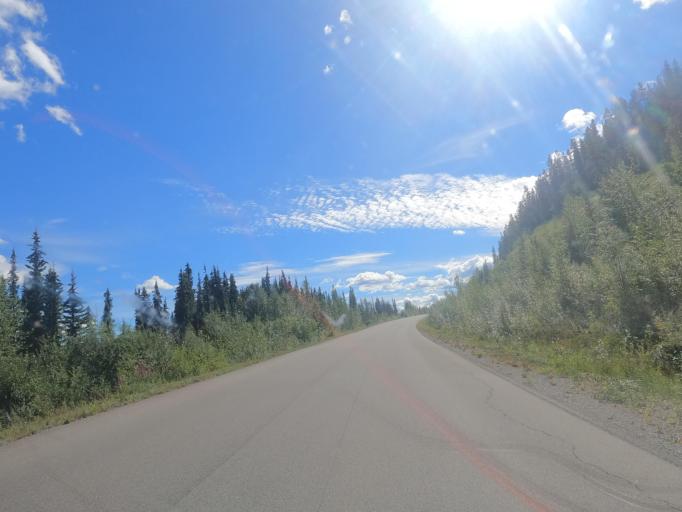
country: CA
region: Yukon
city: Watson Lake
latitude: 59.5930
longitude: -129.2201
